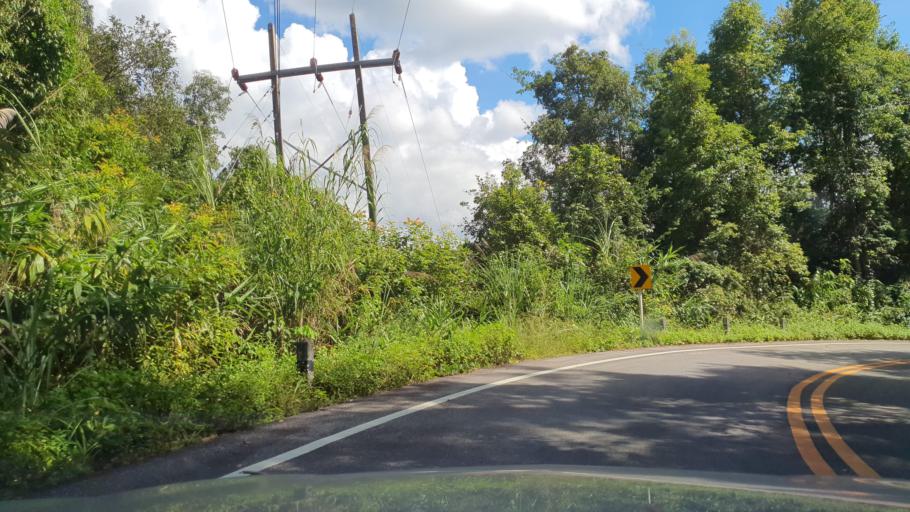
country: TH
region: Chiang Rai
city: Wiang Pa Pao
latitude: 19.3053
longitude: 99.3608
